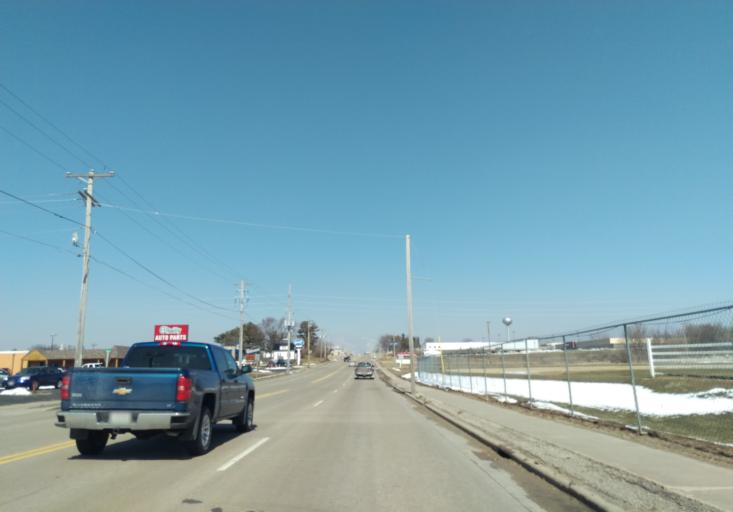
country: US
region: Wisconsin
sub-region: Vernon County
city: Viroqua
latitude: 43.5662
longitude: -90.8889
